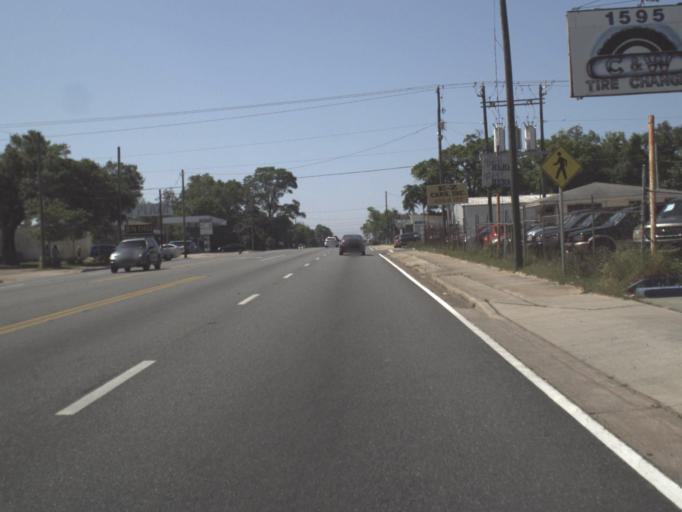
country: US
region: Florida
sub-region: Escambia County
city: Goulding
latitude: 30.4280
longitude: -87.2409
